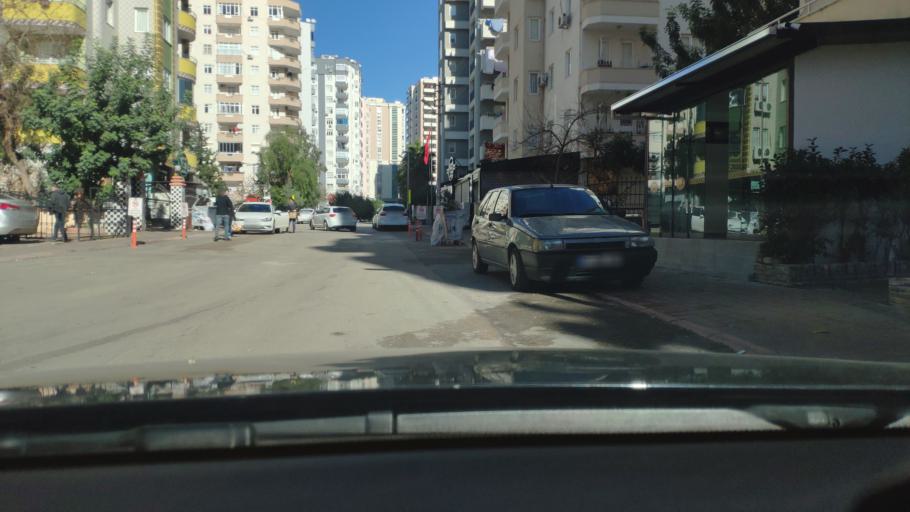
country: TR
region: Adana
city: Adana
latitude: 37.0537
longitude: 35.2815
